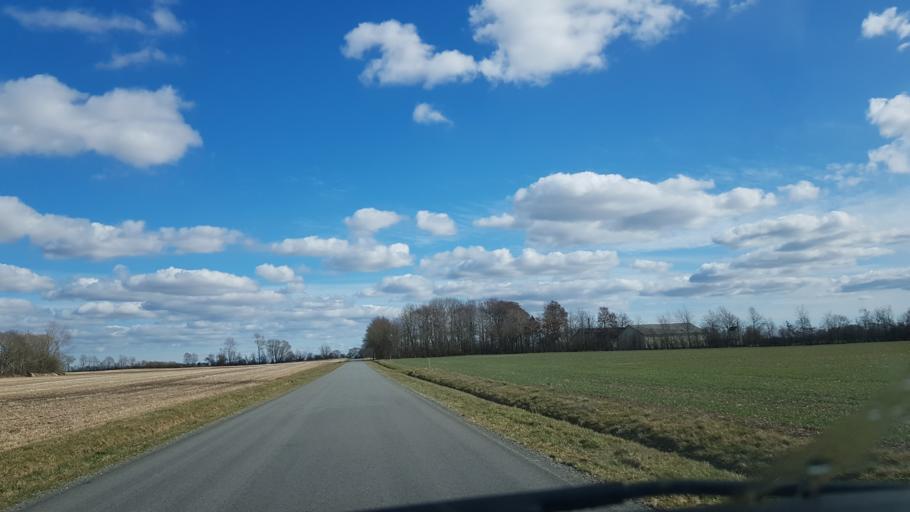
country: DK
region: South Denmark
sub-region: Kolding Kommune
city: Vamdrup
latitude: 55.4097
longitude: 9.2268
